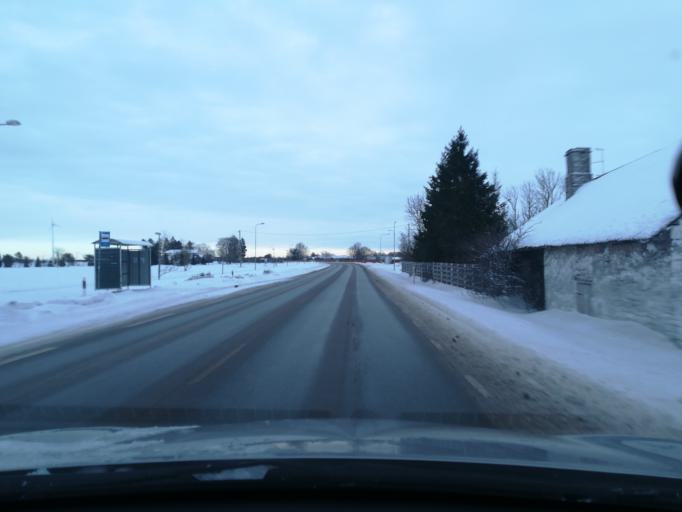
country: EE
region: Harju
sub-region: Harku vald
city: Tabasalu
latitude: 59.4496
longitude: 24.4621
